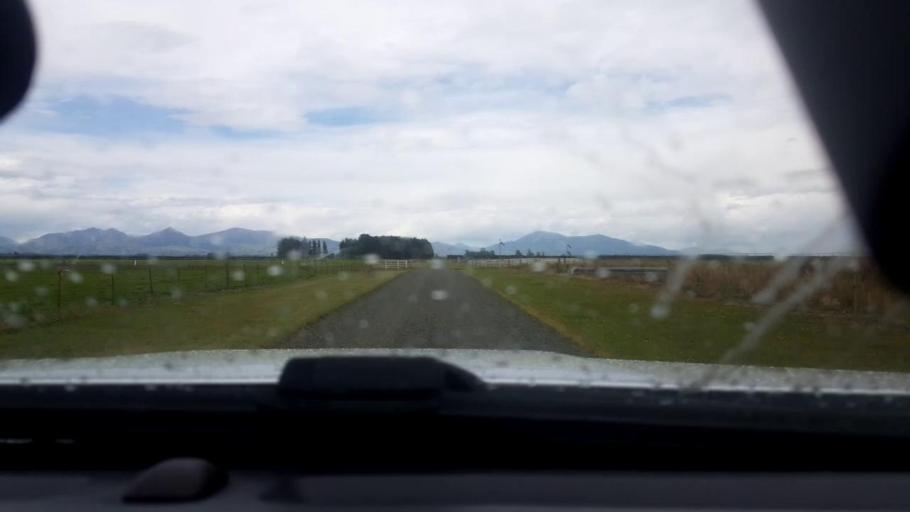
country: NZ
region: Canterbury
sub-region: Timaru District
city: Pleasant Point
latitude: -44.1143
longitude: 171.3549
